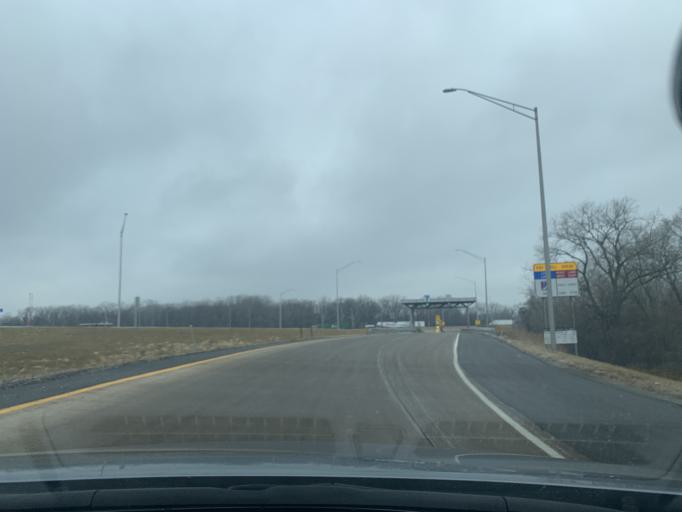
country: US
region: Illinois
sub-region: Cook County
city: University Park
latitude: 41.6013
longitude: -87.6787
